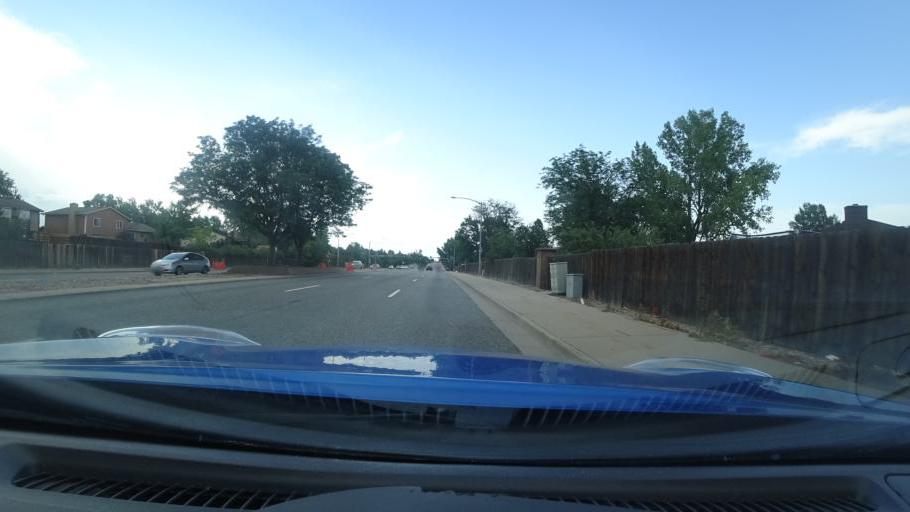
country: US
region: Colorado
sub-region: Adams County
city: Aurora
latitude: 39.6879
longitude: -104.8097
